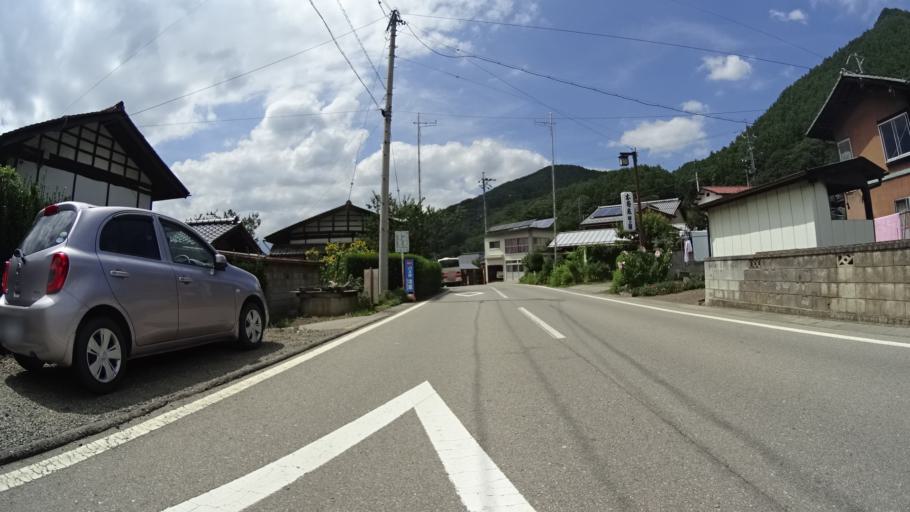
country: JP
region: Nagano
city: Saku
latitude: 36.0593
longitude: 138.5554
